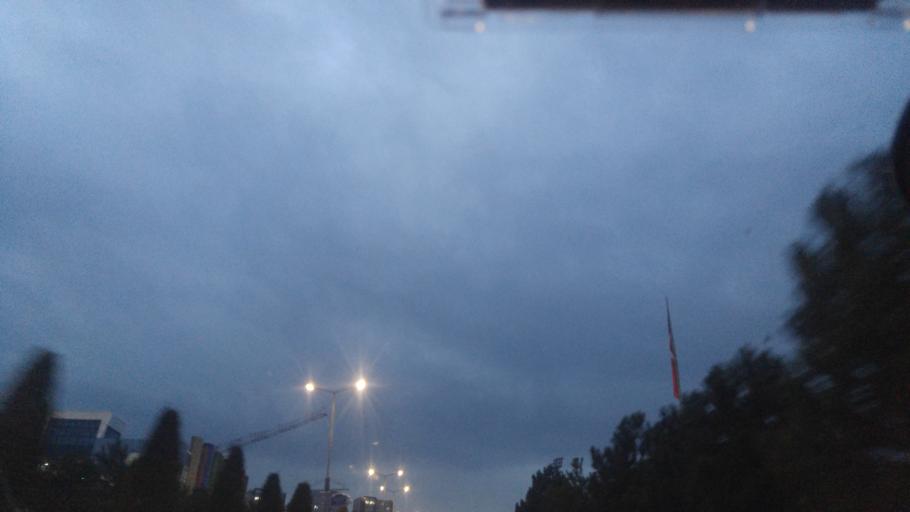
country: TR
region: Karabuk
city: Karabuk
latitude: 41.2088
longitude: 32.6566
